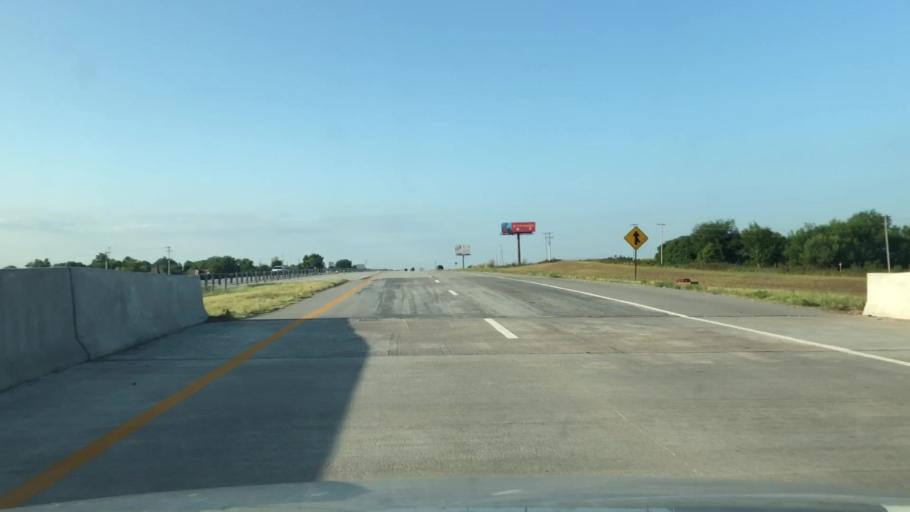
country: US
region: Oklahoma
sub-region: Osage County
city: Skiatook
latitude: 36.3655
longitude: -95.9208
